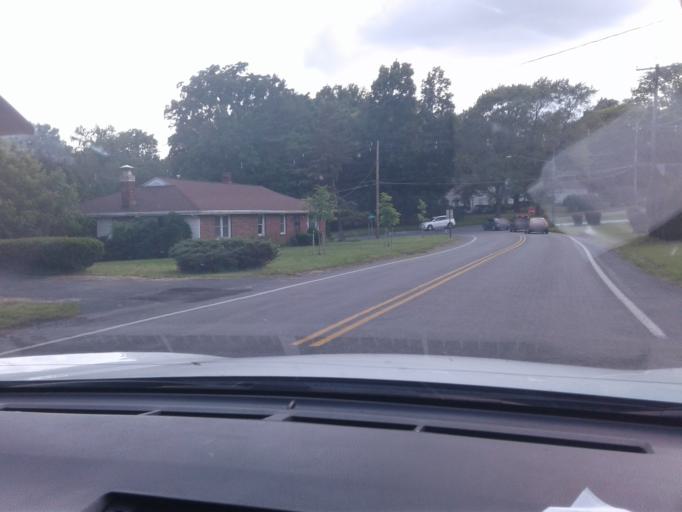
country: US
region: New York
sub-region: Onondaga County
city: East Syracuse
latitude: 43.0477
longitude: -76.0751
